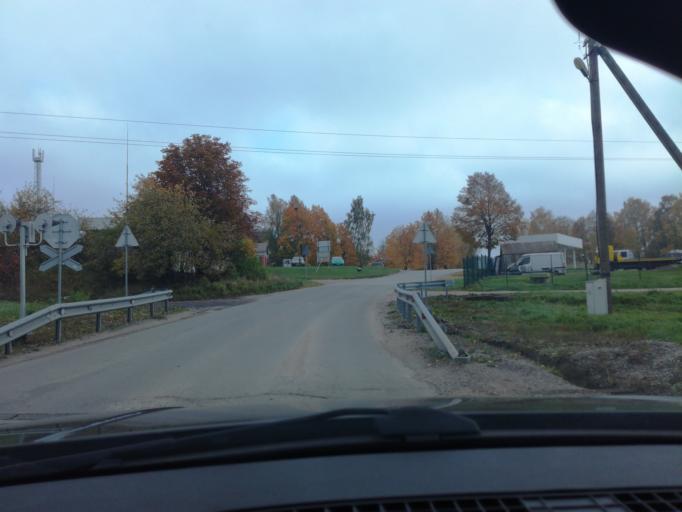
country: LT
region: Alytaus apskritis
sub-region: Alytus
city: Alytus
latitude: 54.4103
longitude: 24.0017
